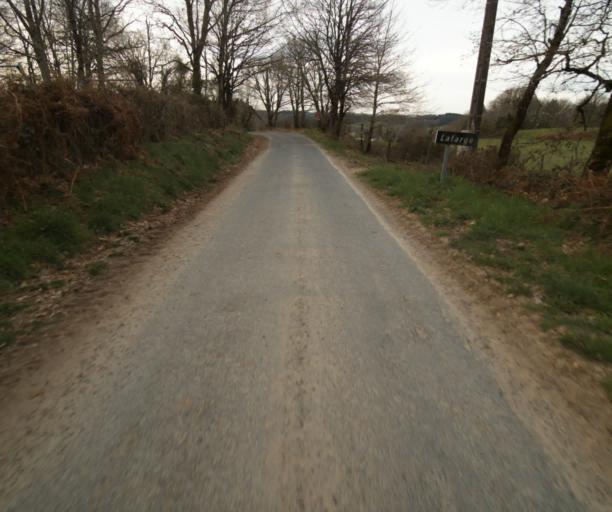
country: FR
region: Limousin
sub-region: Departement de la Correze
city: Correze
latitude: 45.4387
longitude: 1.8230
